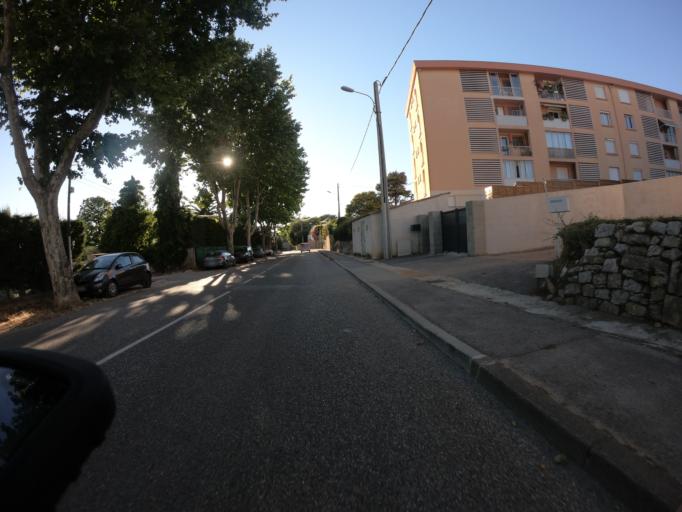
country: FR
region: Provence-Alpes-Cote d'Azur
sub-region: Departement du Var
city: Six-Fours-les-Plages
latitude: 43.1098
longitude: 5.8301
